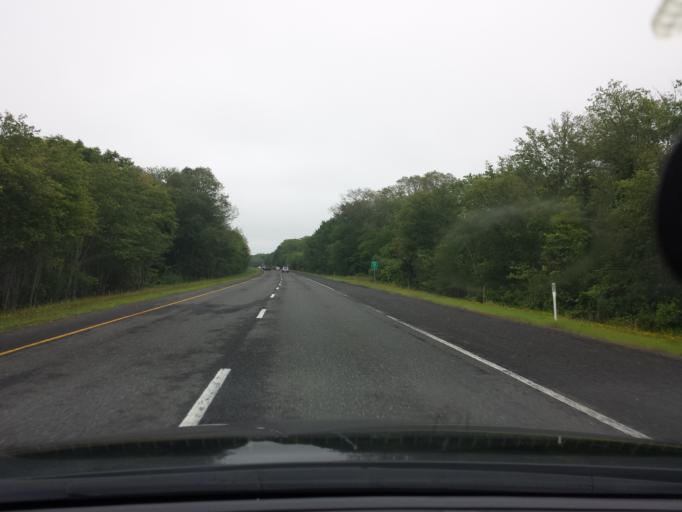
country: US
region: Massachusetts
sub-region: Bristol County
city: Fairhaven
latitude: 41.6598
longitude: -70.8701
